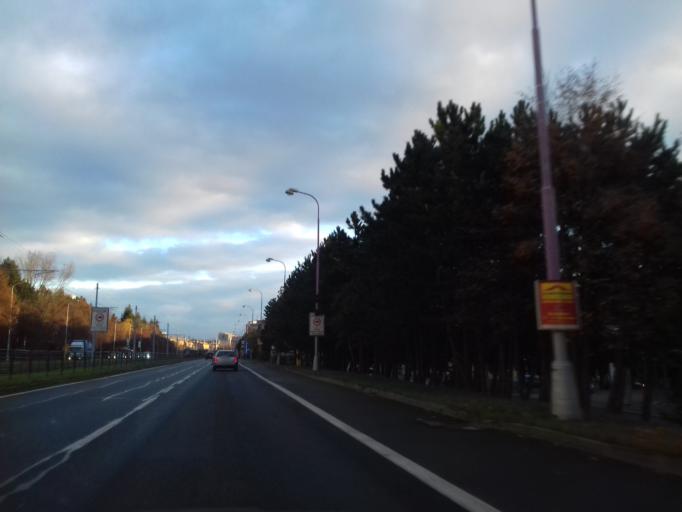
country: CZ
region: Olomoucky
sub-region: Okres Olomouc
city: Olomouc
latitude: 49.5787
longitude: 17.2391
